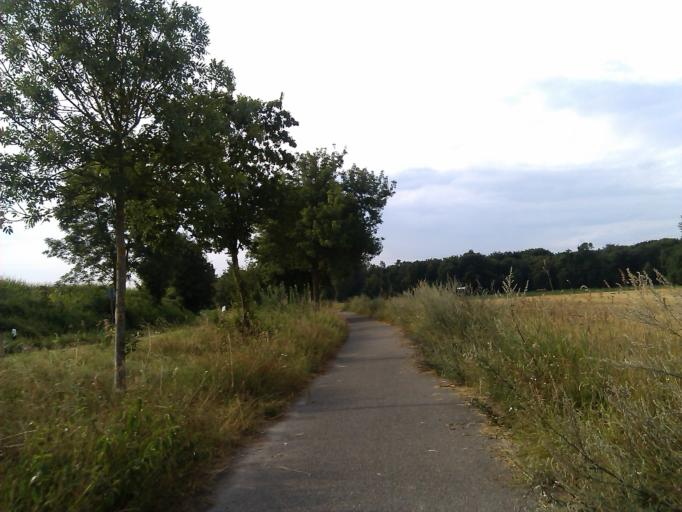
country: DE
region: Rheinland-Pfalz
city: Altrip
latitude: 49.4247
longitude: 8.4780
